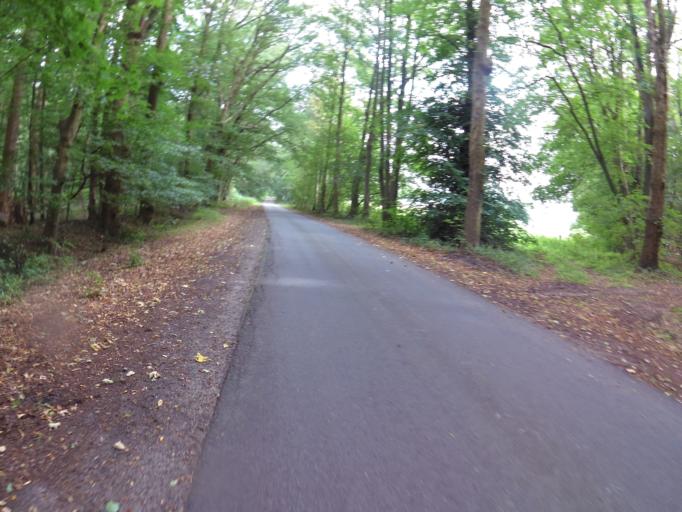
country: DE
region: Lower Saxony
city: Kohlen
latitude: 53.5059
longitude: 8.9067
